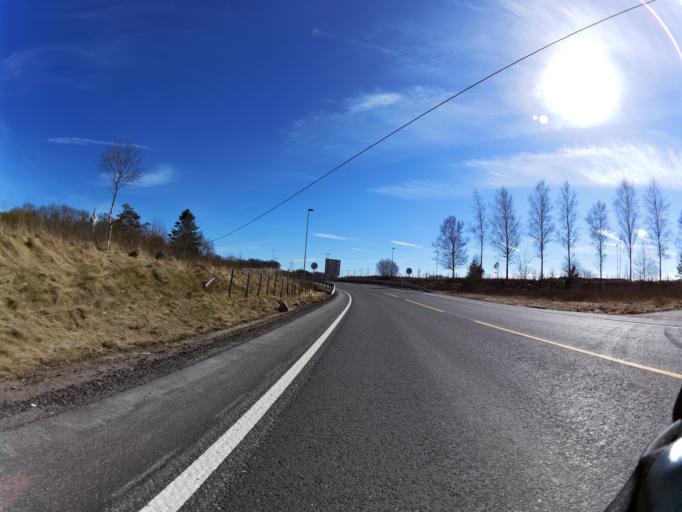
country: NO
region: Ostfold
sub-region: Rade
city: Karlshus
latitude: 59.3259
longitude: 10.9588
